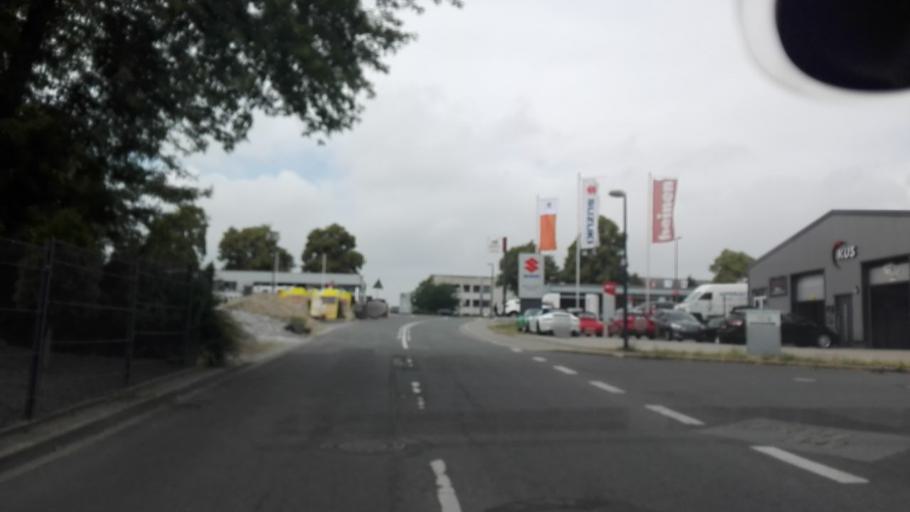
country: DE
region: North Rhine-Westphalia
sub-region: Regierungsbezirk Arnsberg
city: Holzwickede
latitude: 51.5160
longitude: 7.6200
